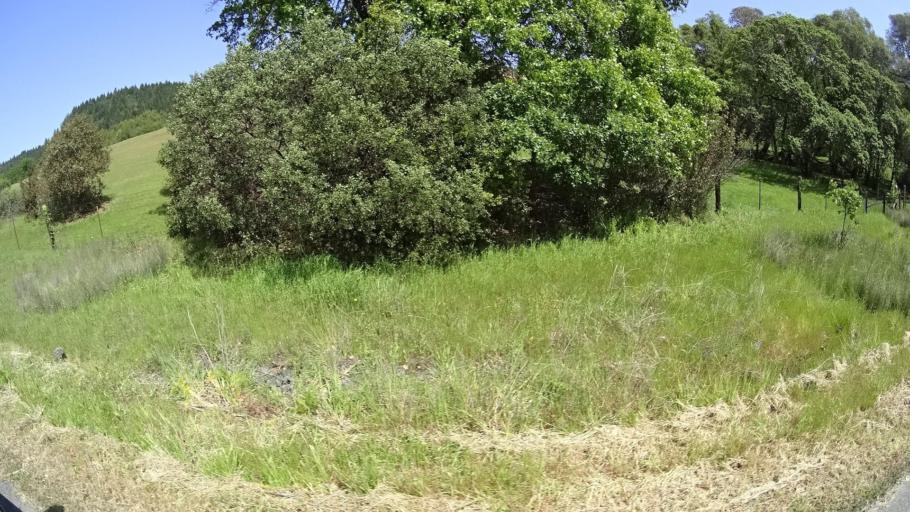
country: US
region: California
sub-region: Humboldt County
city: Redway
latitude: 40.2523
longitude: -123.6241
